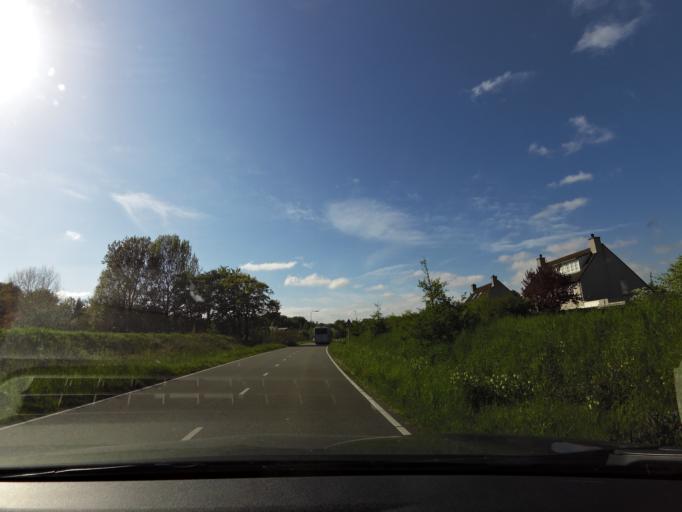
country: NL
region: South Holland
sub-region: Gemeente Hellevoetsluis
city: Nieuw-Helvoet
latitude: 51.8675
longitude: 4.0656
